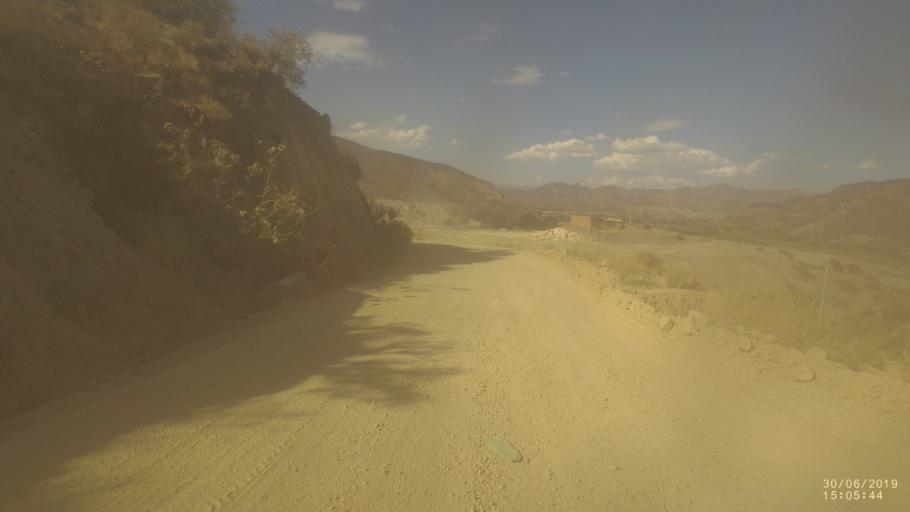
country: BO
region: Cochabamba
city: Irpa Irpa
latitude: -17.7328
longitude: -66.3153
